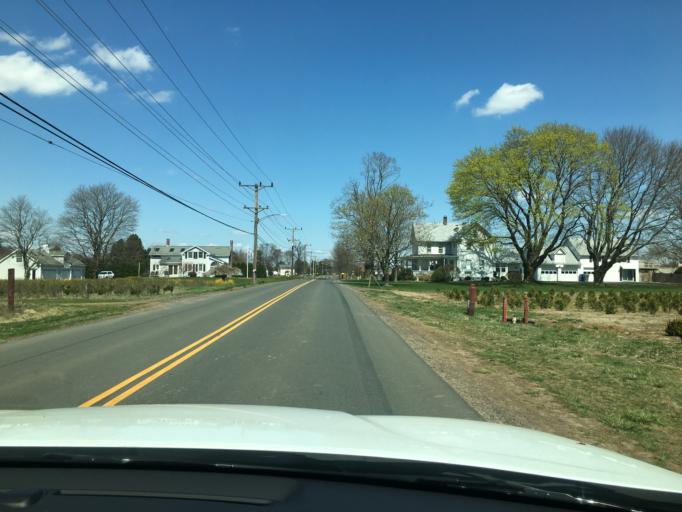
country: US
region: Connecticut
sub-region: Hartford County
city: Hazardville
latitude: 41.9919
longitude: -72.5290
